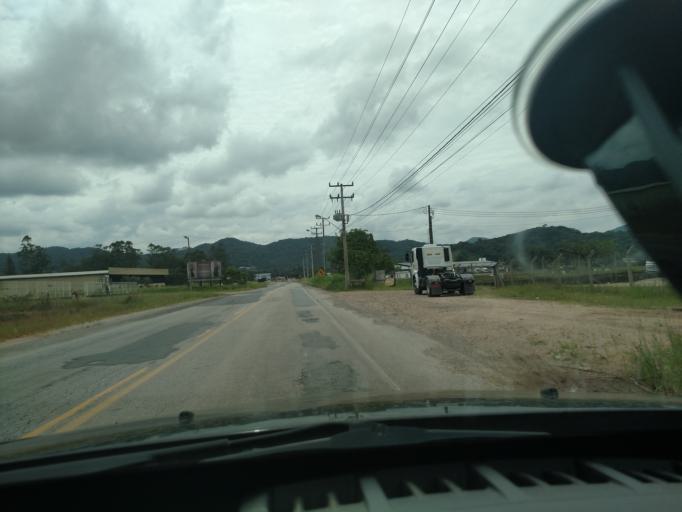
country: BR
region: Santa Catarina
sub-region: Gaspar
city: Gaspar
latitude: -26.9160
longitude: -48.9340
